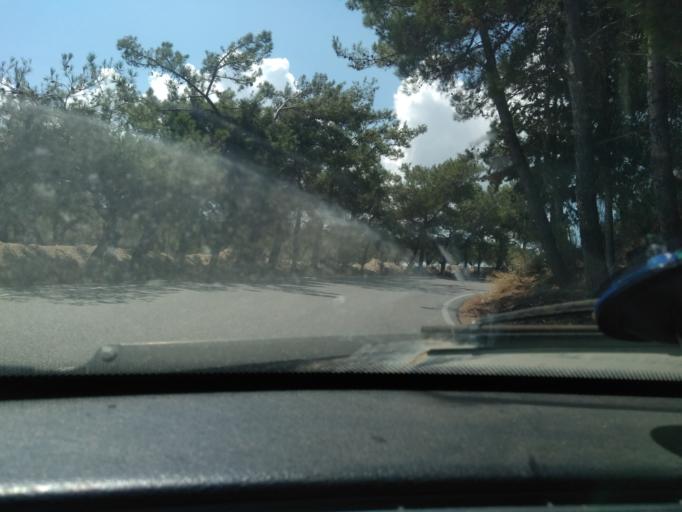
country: GR
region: Crete
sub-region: Nomos Lasithiou
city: Siteia
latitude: 35.1296
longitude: 26.0740
